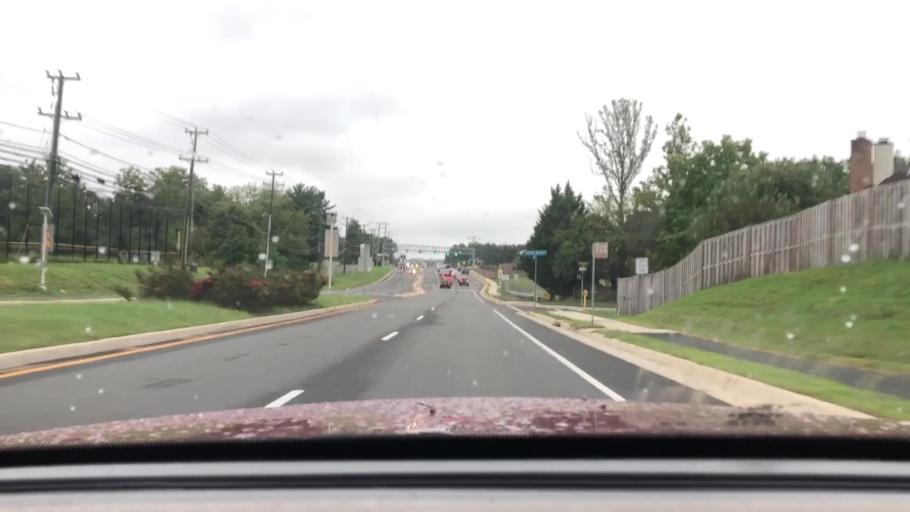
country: US
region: Virginia
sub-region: Fairfax County
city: Greenbriar
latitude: 38.8783
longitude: -77.4091
